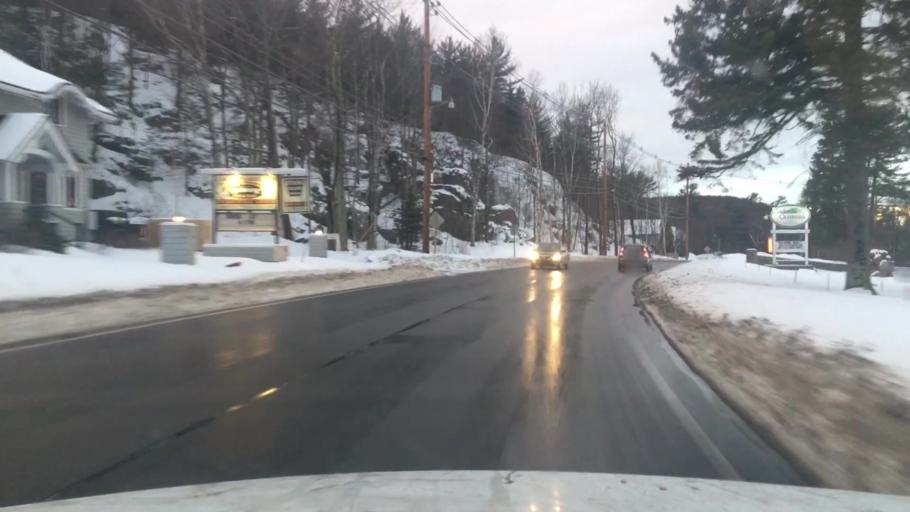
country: US
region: Maine
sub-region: Hancock County
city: Bar Harbor
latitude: 44.3963
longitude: -68.2262
